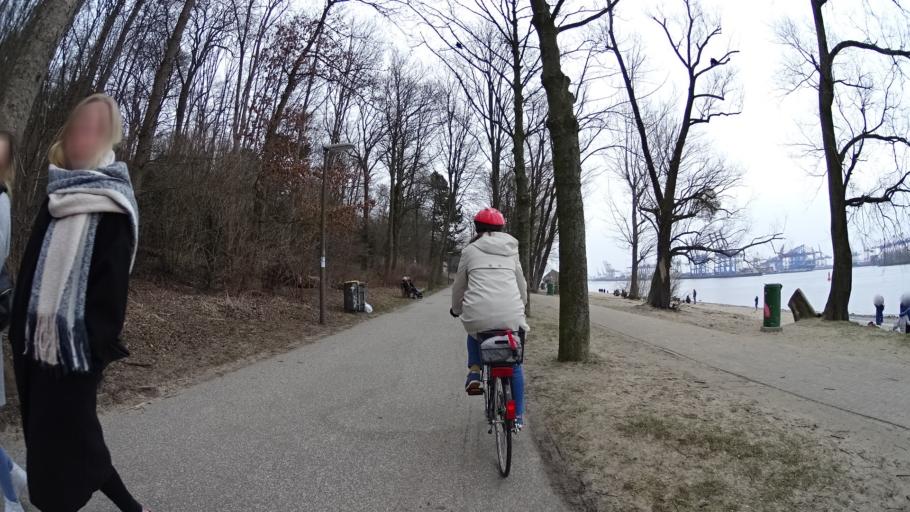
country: DE
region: Hamburg
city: Altona
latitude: 53.5448
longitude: 9.8941
